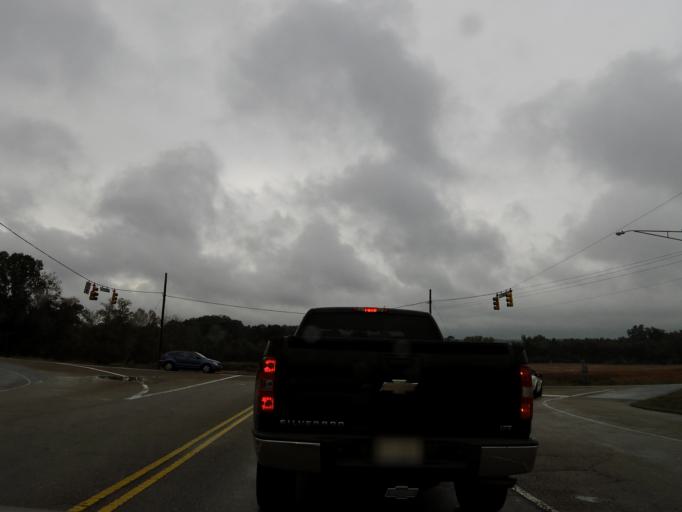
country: US
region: Tennessee
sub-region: Bradley County
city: Hopewell
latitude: 35.2135
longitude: -84.8821
